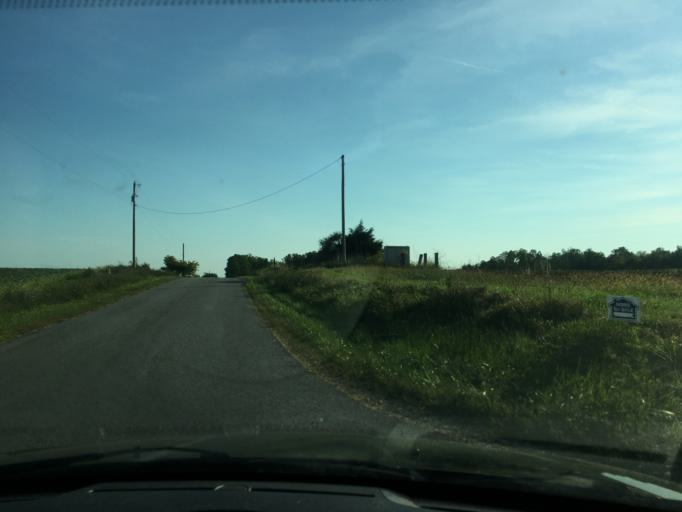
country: US
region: Ohio
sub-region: Logan County
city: West Liberty
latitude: 40.2498
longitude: -83.6650
